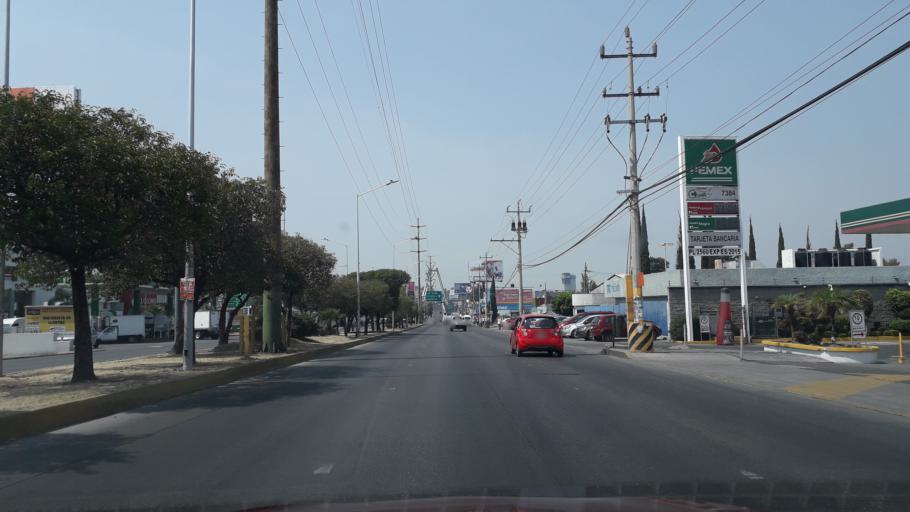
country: MX
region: Puebla
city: Puebla
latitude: 19.0690
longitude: -98.1759
